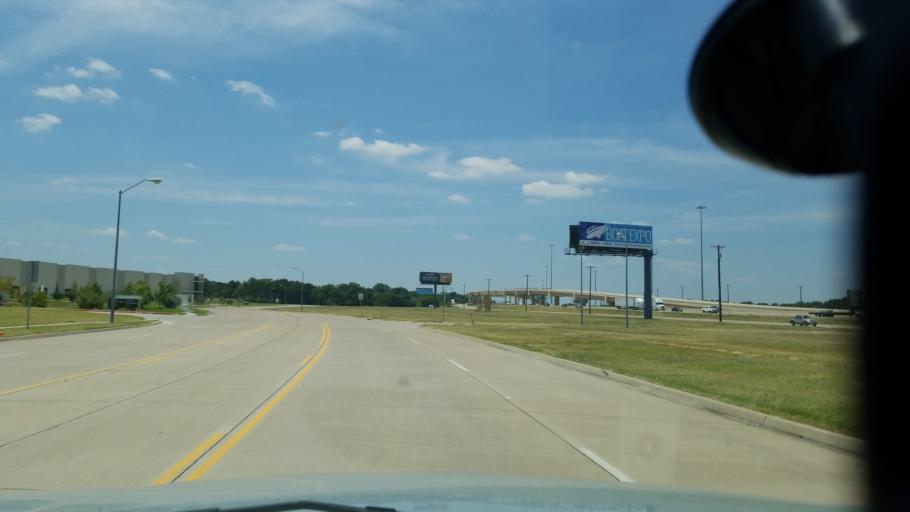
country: US
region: Texas
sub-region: Dallas County
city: Grand Prairie
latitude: 32.7605
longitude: -96.9665
